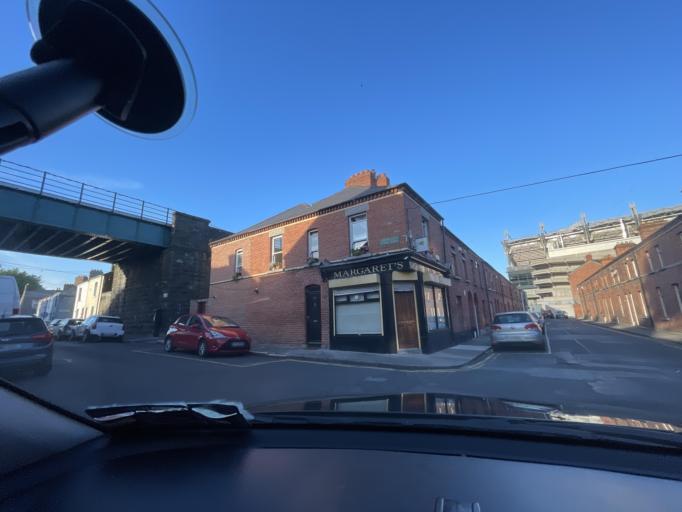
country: IE
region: Leinster
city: Drumcondra
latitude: 53.3618
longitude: -6.2544
